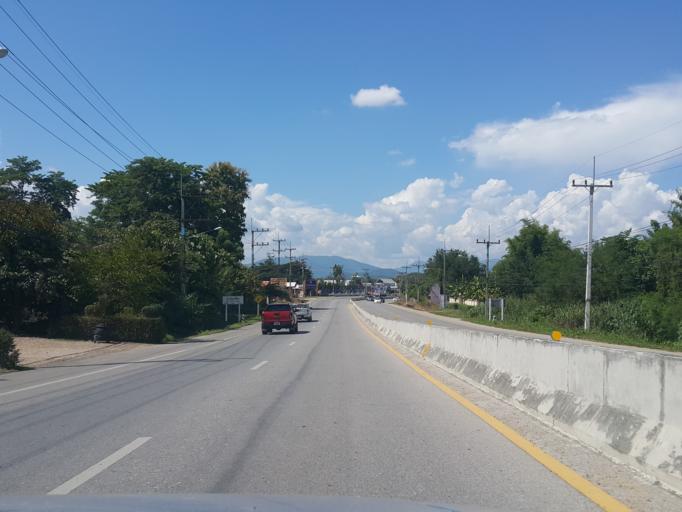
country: TH
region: Chiang Mai
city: Mae Taeng
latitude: 19.0600
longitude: 98.9404
